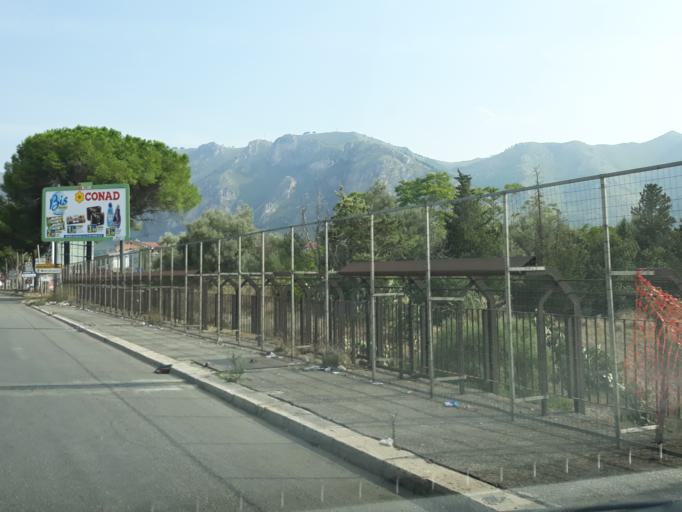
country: IT
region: Sicily
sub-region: Palermo
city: Villa Ciambra
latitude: 38.0898
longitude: 13.3445
